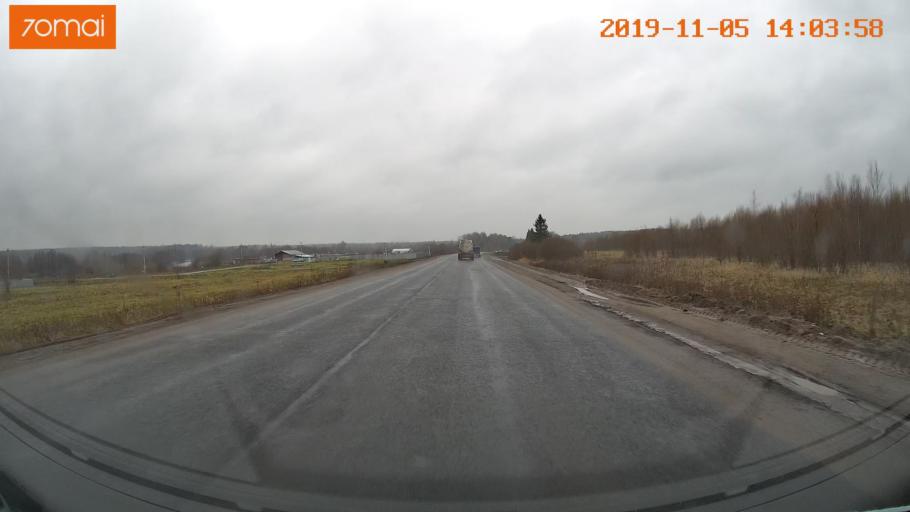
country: RU
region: Ivanovo
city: Kokhma
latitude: 56.9975
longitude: 41.1856
